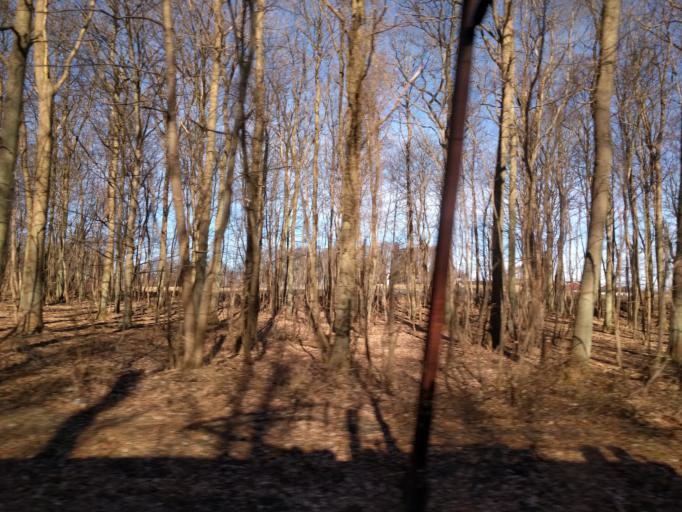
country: DK
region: Capital Region
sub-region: Helsingor Kommune
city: Espergaerde
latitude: 56.0006
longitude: 12.5547
